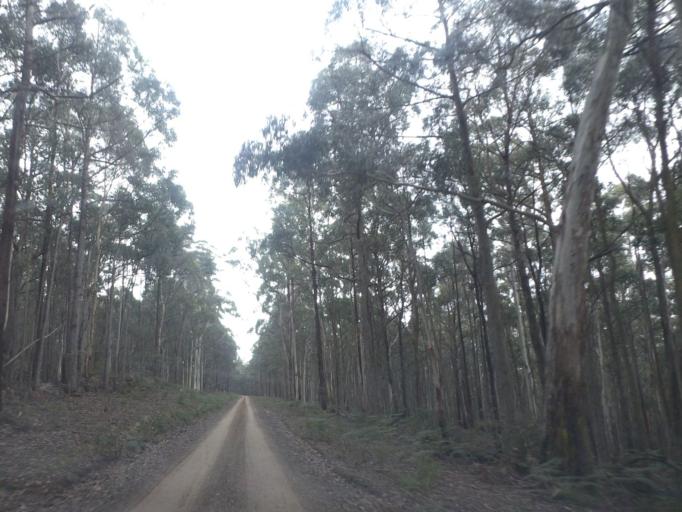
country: AU
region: Victoria
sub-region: Moorabool
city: Bacchus Marsh
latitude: -37.4360
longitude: 144.3191
